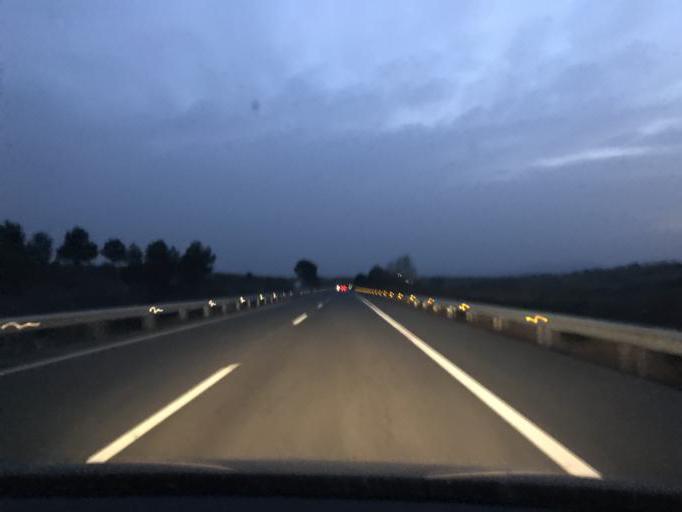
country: ES
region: Andalusia
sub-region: Provincia de Granada
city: Gor
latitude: 37.3937
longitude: -2.9653
